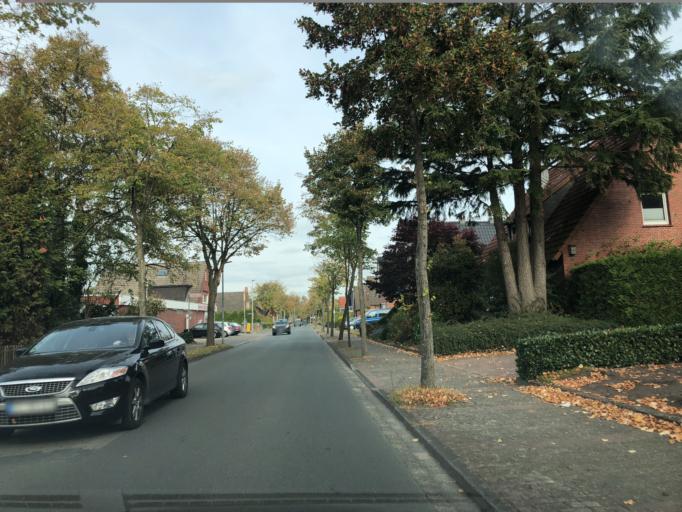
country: DE
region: Lower Saxony
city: Papenburg
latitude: 53.0676
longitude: 7.4082
